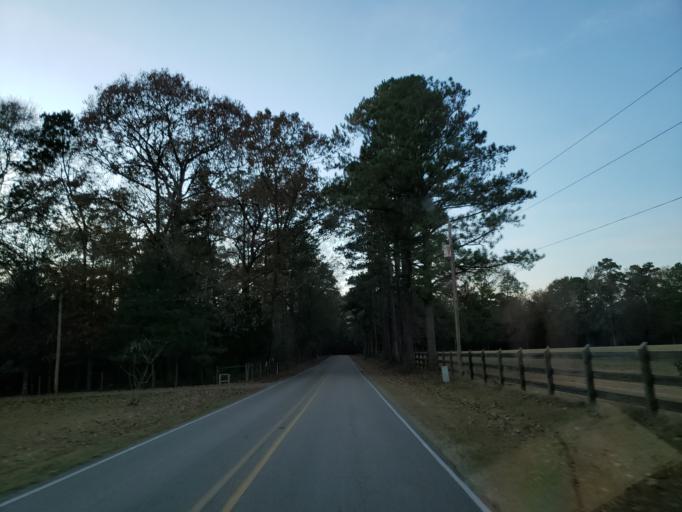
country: US
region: Mississippi
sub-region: Forrest County
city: Hattiesburg
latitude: 31.2419
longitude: -89.3147
